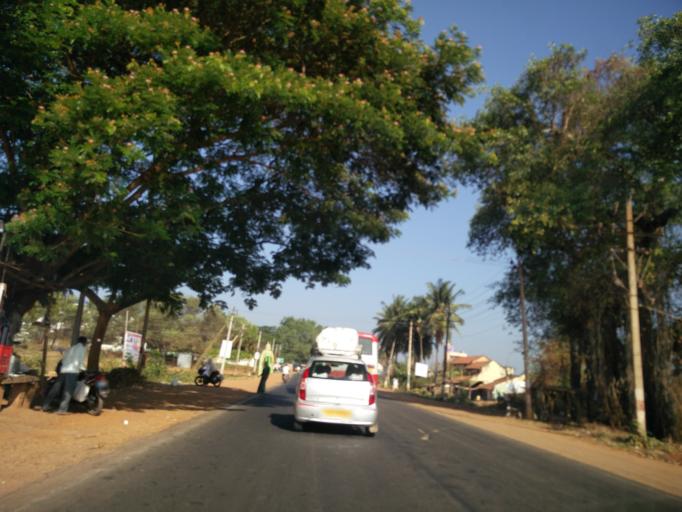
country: IN
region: Karnataka
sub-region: Tumkur
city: Gubbi
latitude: 13.3087
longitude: 76.9259
